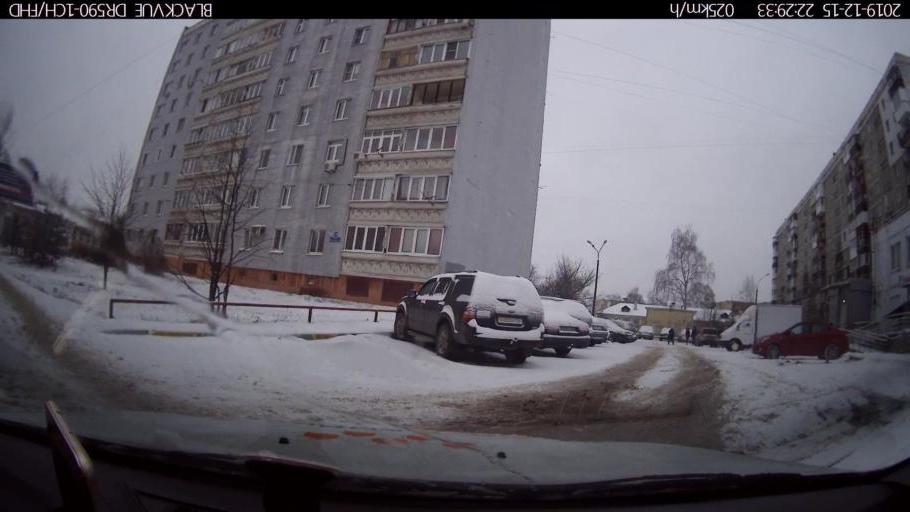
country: RU
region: Nizjnij Novgorod
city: Gorbatovka
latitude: 56.3490
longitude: 43.8509
